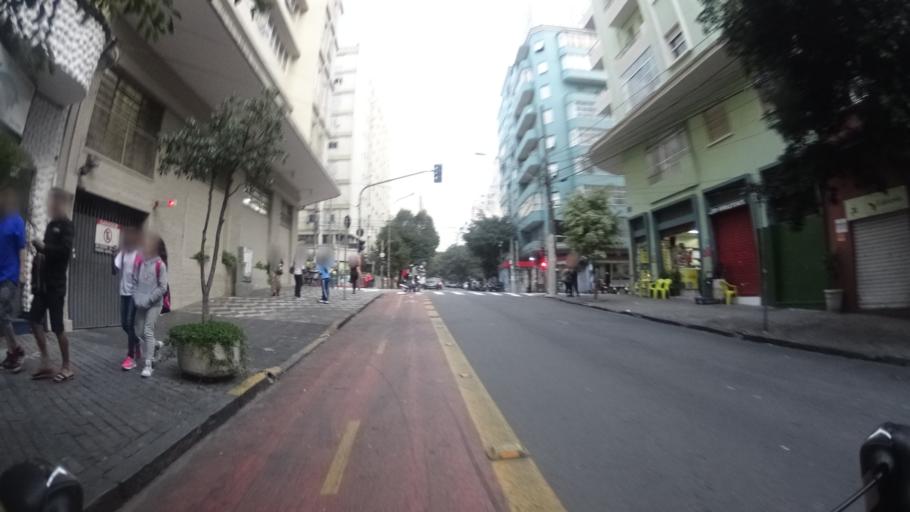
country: BR
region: Sao Paulo
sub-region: Sao Paulo
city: Sao Paulo
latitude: -23.5388
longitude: -46.6513
